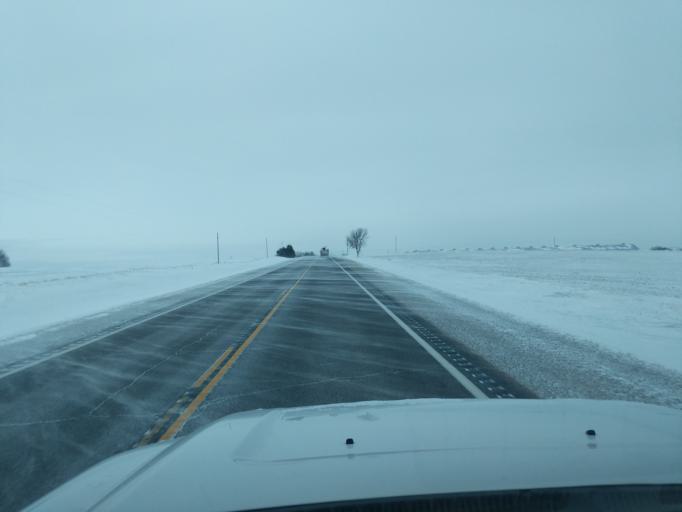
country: US
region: Minnesota
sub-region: Redwood County
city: Redwood Falls
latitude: 44.6100
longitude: -94.9945
